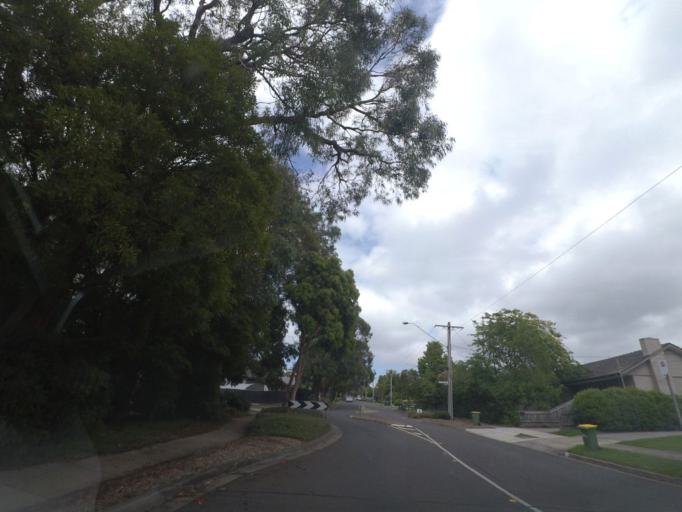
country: AU
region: Victoria
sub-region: Knox
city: Boronia
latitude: -37.8725
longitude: 145.2797
